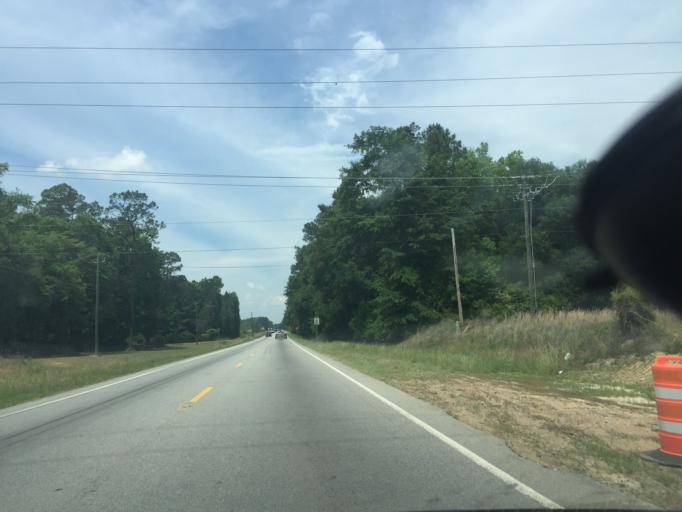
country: US
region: Georgia
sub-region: Chatham County
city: Bloomingdale
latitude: 32.1584
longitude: -81.3649
